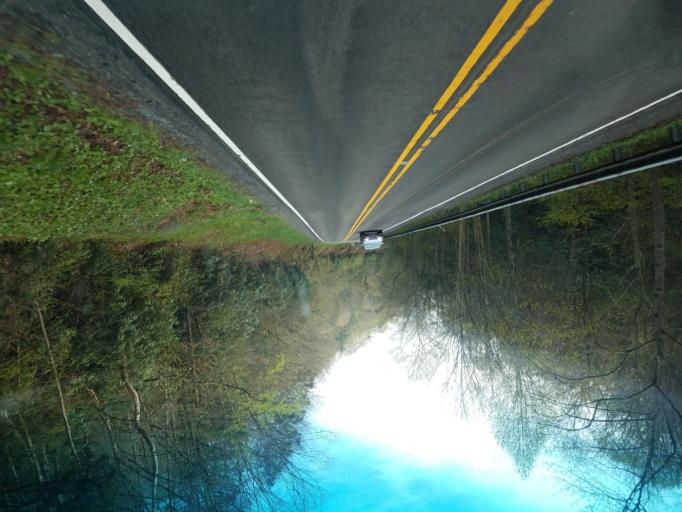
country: US
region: Virginia
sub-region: Smyth County
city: Atkins
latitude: 36.8016
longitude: -81.4044
